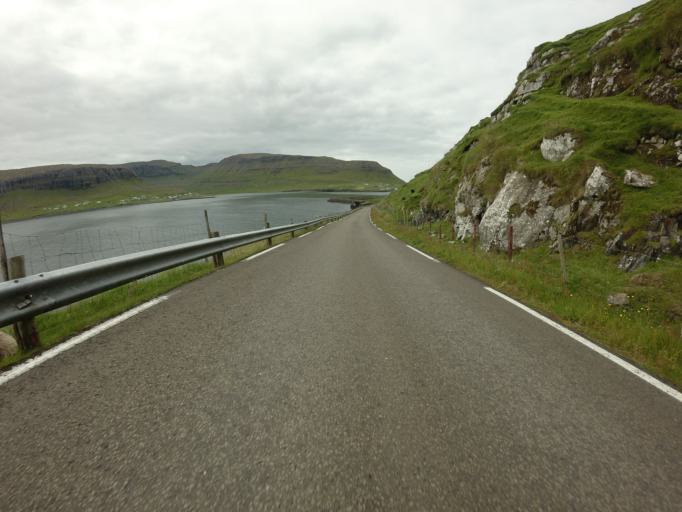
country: FO
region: Suduroy
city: Tvoroyri
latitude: 61.6072
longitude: -6.9301
